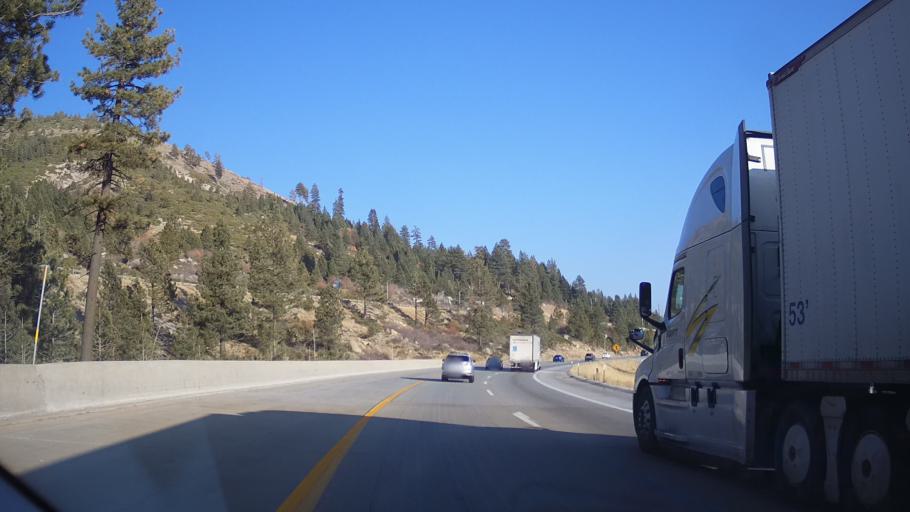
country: US
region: California
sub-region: Nevada County
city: Truckee
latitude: 39.3310
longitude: -120.2892
